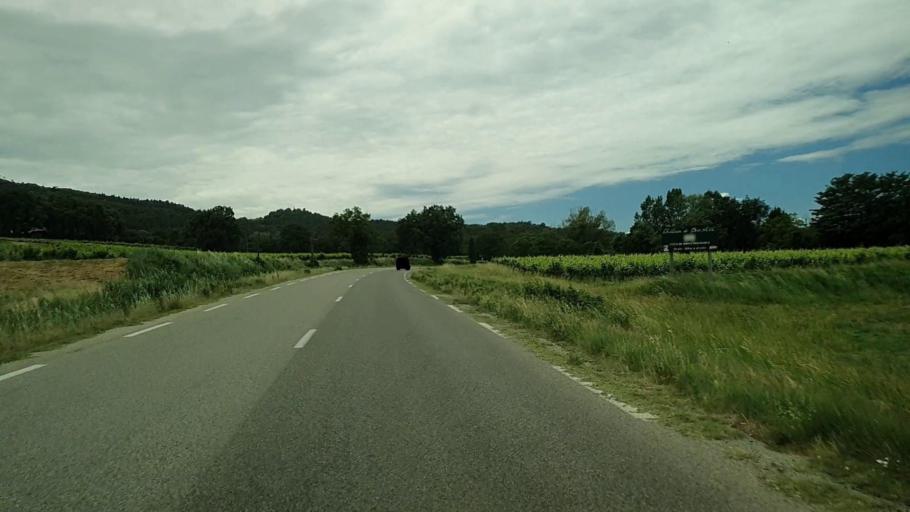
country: FR
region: Languedoc-Roussillon
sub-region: Departement du Gard
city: Sabran
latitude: 44.1639
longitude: 4.5655
